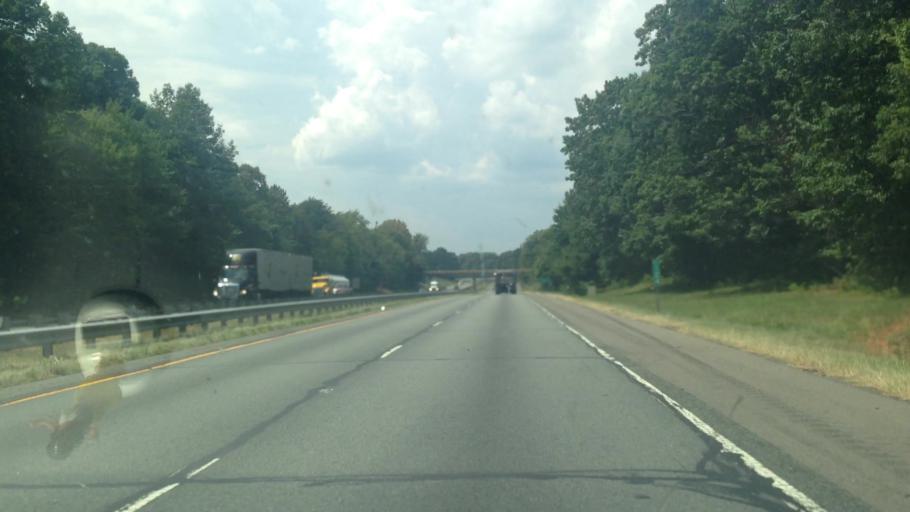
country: US
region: North Carolina
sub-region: Stokes County
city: King
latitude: 36.2699
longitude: -80.3743
